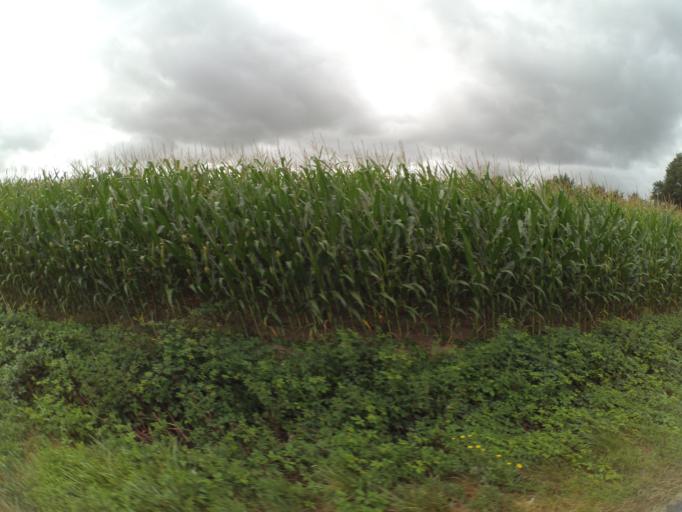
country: FR
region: Pays de la Loire
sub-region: Departement de Maine-et-Loire
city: Villedieu-la-Blouere
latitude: 47.1347
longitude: -1.0793
